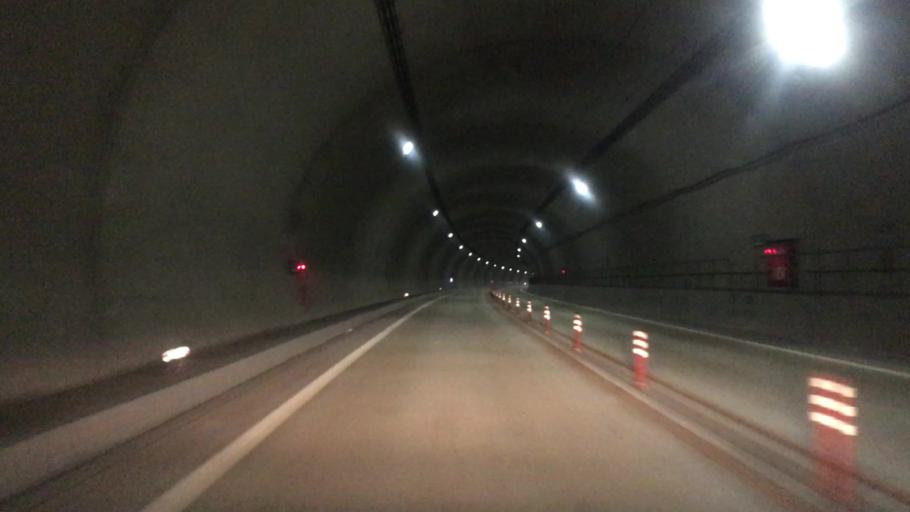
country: JP
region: Tottori
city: Tottori
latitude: 35.5647
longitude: 134.2871
